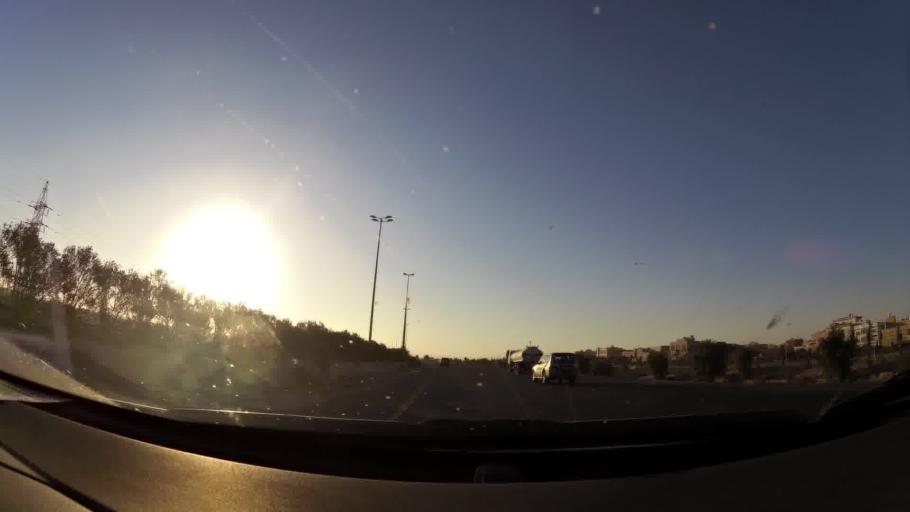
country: KW
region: Al Ahmadi
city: Al Fahahil
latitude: 28.9614
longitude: 48.1669
